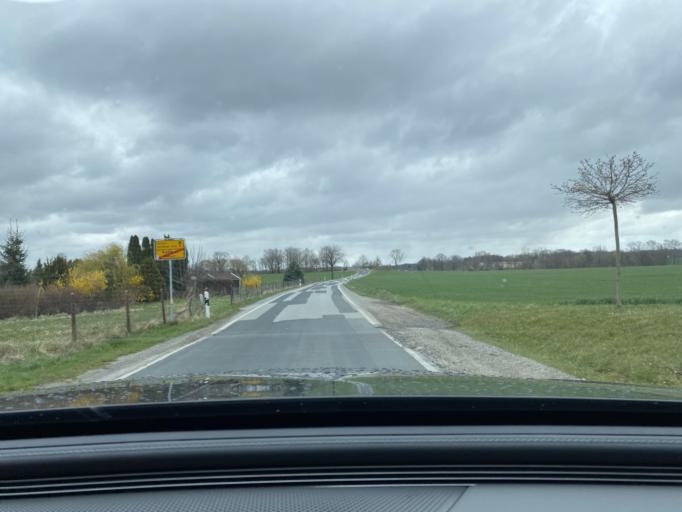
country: DE
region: Saxony
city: Radibor
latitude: 51.2461
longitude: 14.4037
